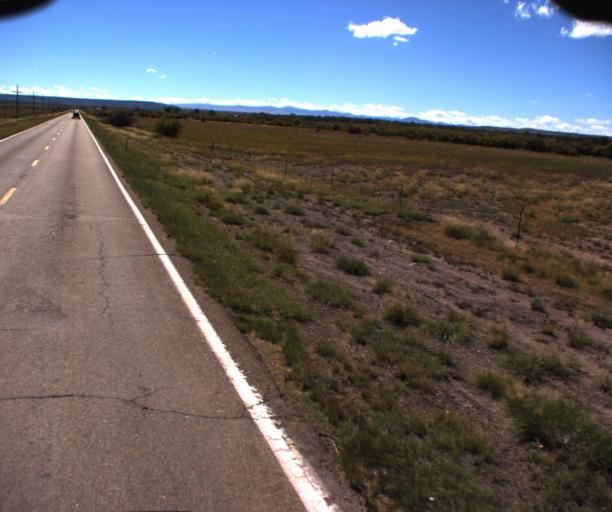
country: US
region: Arizona
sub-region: Apache County
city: Saint Johns
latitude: 34.5285
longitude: -109.3460
